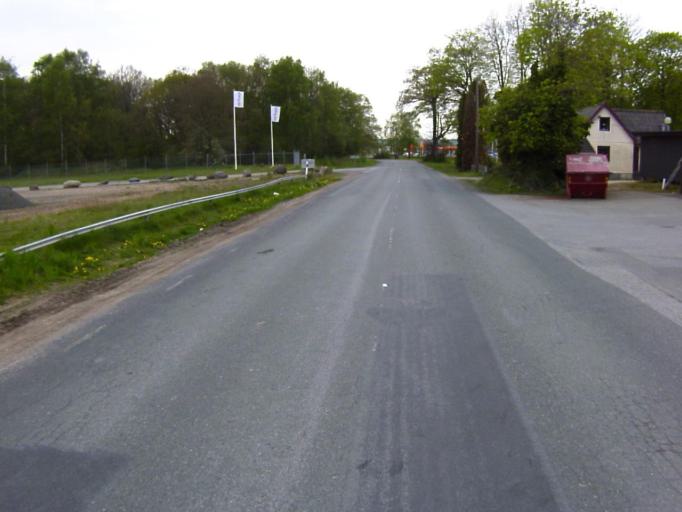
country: SE
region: Skane
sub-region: Kristianstads Kommun
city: Onnestad
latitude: 55.9319
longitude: 13.9934
